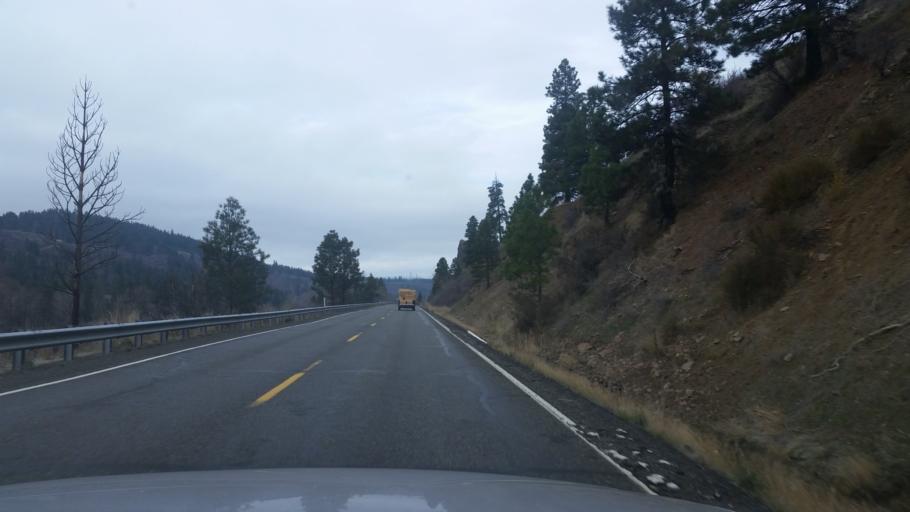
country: US
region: Washington
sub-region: Kittitas County
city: Cle Elum
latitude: 47.1344
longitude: -120.7865
